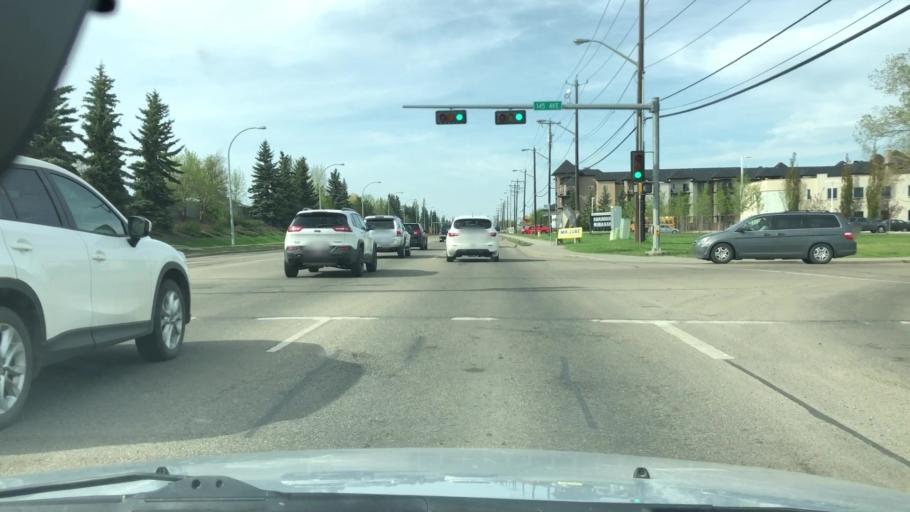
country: CA
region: Alberta
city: Edmonton
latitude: 53.6065
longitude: -113.5412
